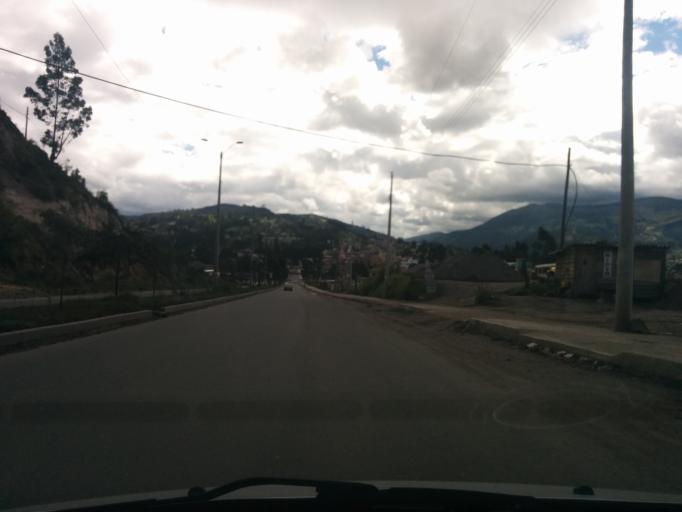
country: EC
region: Azuay
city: Cuenca
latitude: -2.9236
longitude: -79.0338
